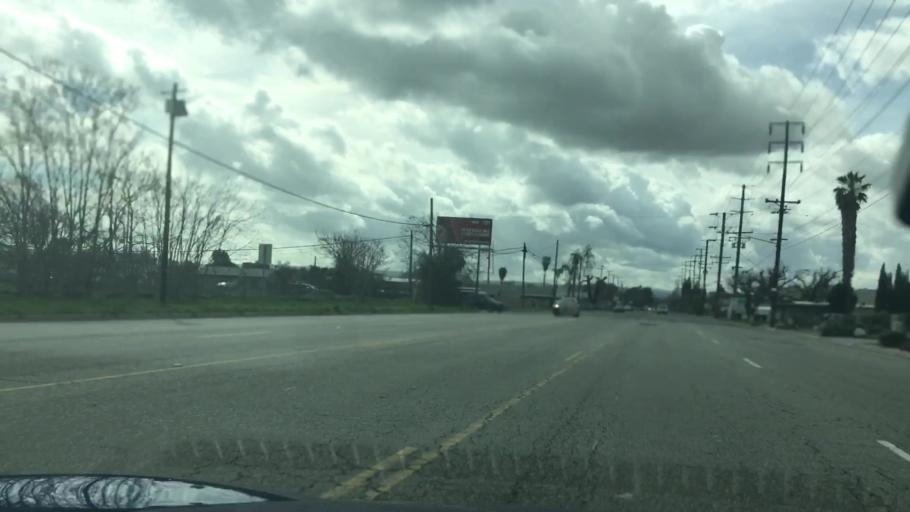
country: US
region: California
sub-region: Riverside County
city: Highgrove
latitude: 34.0200
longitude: -117.3625
